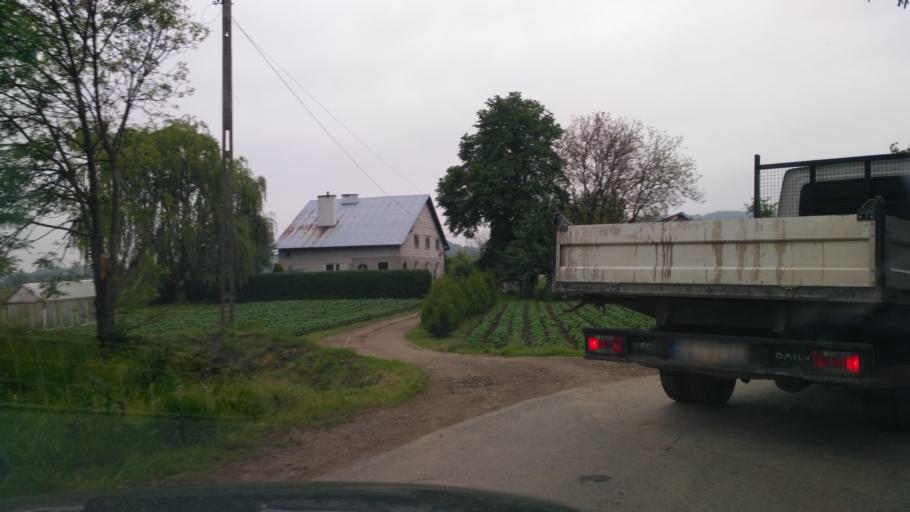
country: PL
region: Subcarpathian Voivodeship
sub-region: Powiat rzeszowski
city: Dynow
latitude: 49.8105
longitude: 22.2371
